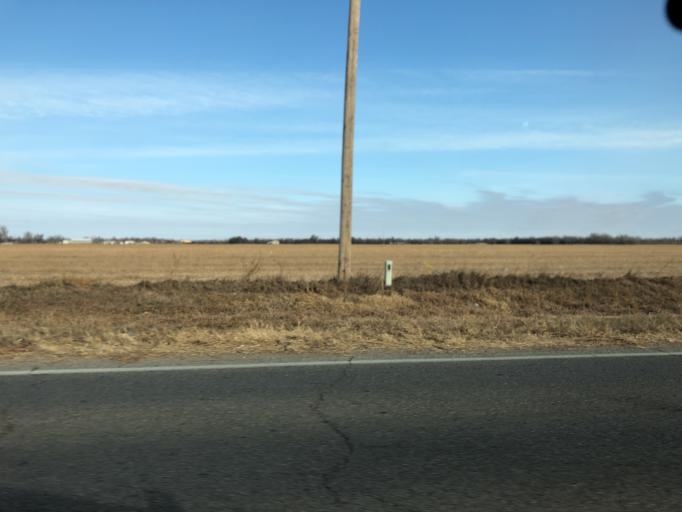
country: US
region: Kansas
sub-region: Reno County
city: Hutchinson
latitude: 38.0571
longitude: -97.9742
